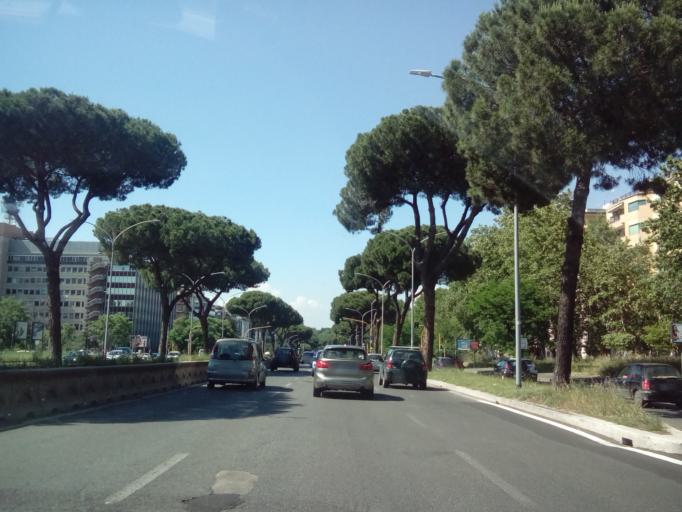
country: IT
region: Latium
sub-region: Citta metropolitana di Roma Capitale
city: Rome
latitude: 41.8627
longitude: 12.4978
